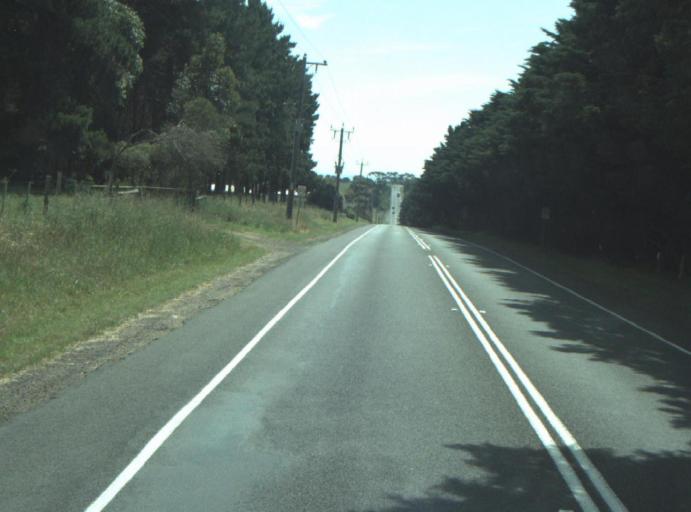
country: AU
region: Victoria
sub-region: Greater Geelong
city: Clifton Springs
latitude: -38.1519
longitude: 144.5916
